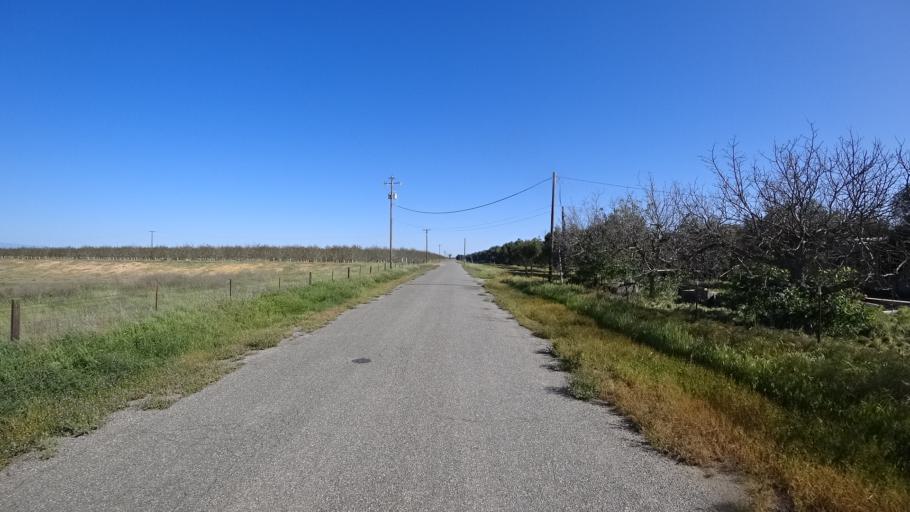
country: US
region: California
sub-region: Glenn County
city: Hamilton City
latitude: 39.6804
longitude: -122.0743
